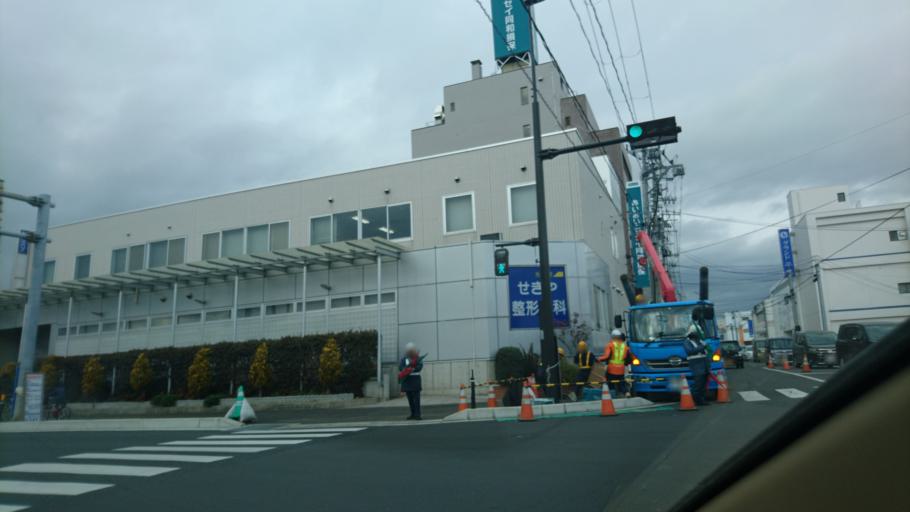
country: JP
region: Miyagi
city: Furukawa
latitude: 38.5763
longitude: 140.9655
